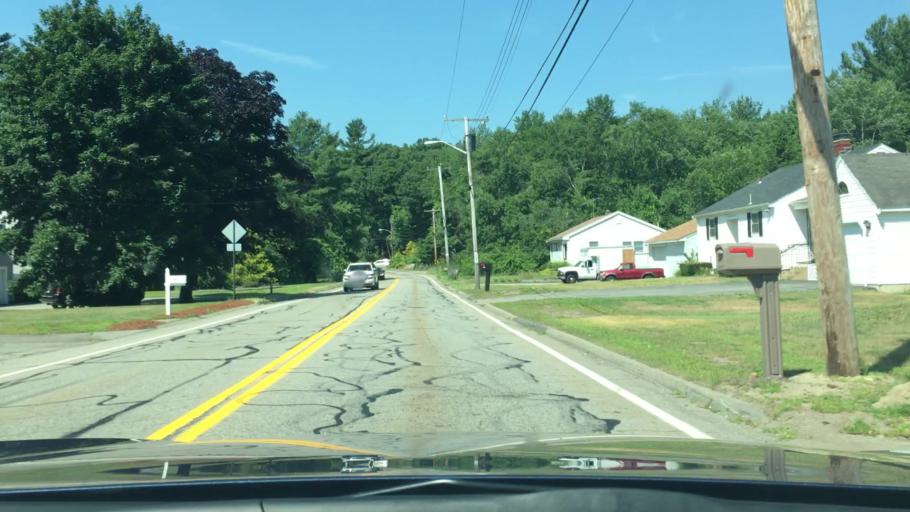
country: US
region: Massachusetts
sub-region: Middlesex County
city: Billerica
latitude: 42.5727
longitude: -71.2927
